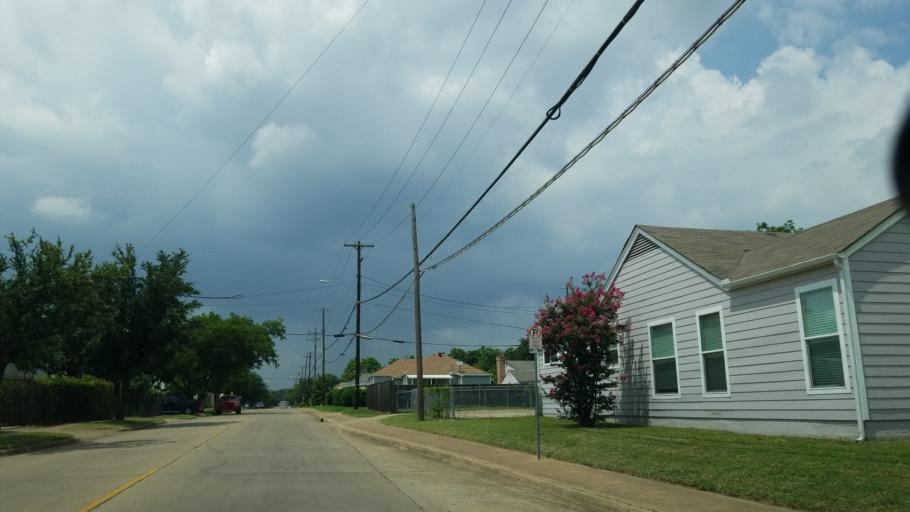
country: US
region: Texas
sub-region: Dallas County
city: University Park
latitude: 32.8450
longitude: -96.8301
